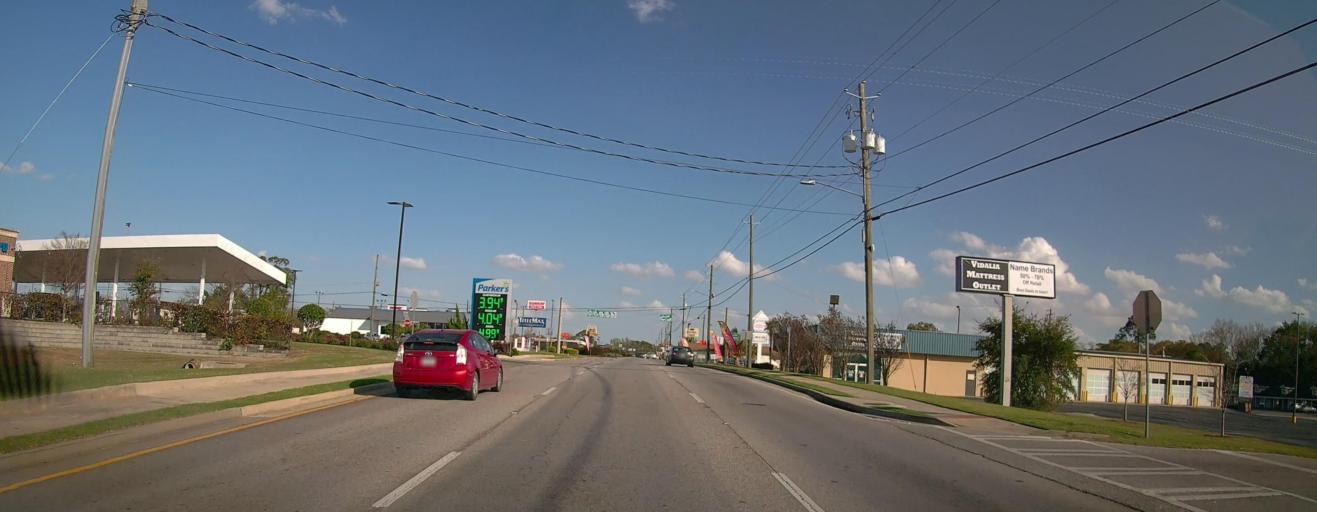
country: US
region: Georgia
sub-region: Toombs County
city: Vidalia
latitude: 32.2147
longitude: -82.4064
